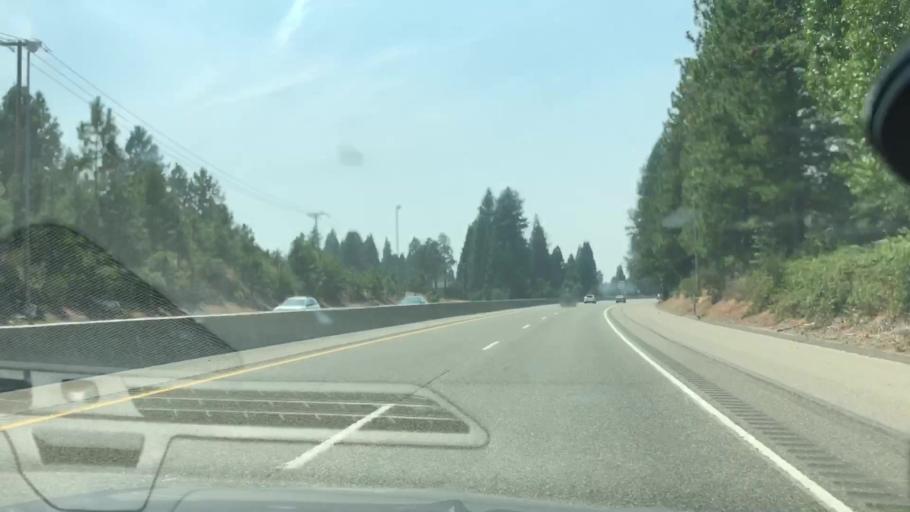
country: US
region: California
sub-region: El Dorado County
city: Camino
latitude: 38.7378
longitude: -120.7032
